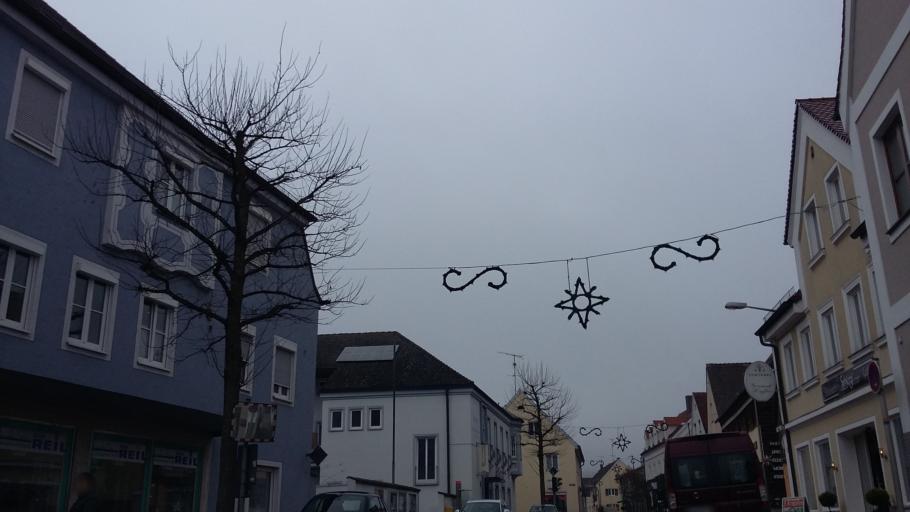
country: DE
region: Bavaria
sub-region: Swabia
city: Pottmes
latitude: 48.5844
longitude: 11.0902
